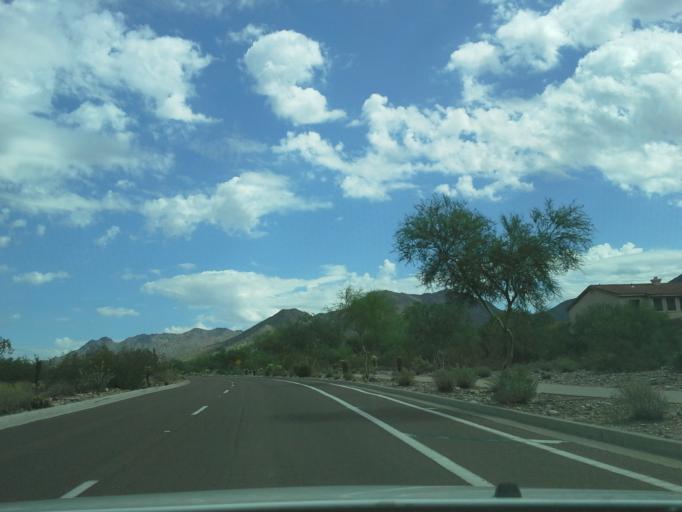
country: US
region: Arizona
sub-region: Maricopa County
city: Scottsdale
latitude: 33.6304
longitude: -111.8617
